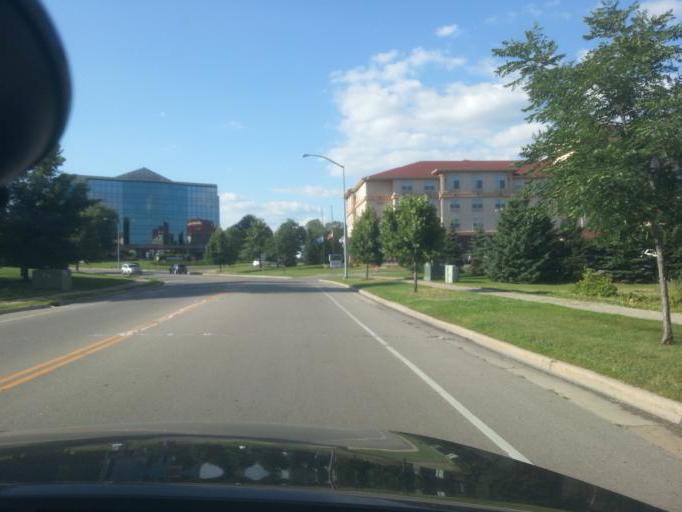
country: US
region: Wisconsin
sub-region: Dane County
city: Middleton
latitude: 43.0810
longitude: -89.5242
